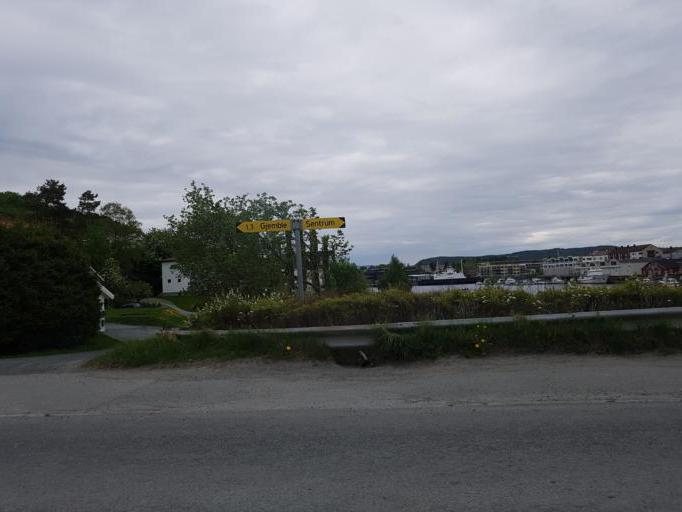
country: NO
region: Nord-Trondelag
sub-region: Levanger
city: Levanger
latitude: 63.7468
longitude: 11.2928
